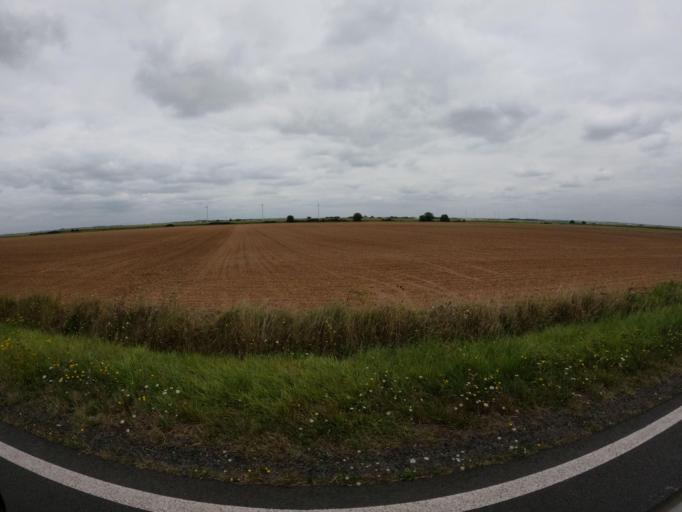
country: FR
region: Pays de la Loire
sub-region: Departement de la Vendee
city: Maillezais
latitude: 46.4287
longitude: -0.7250
